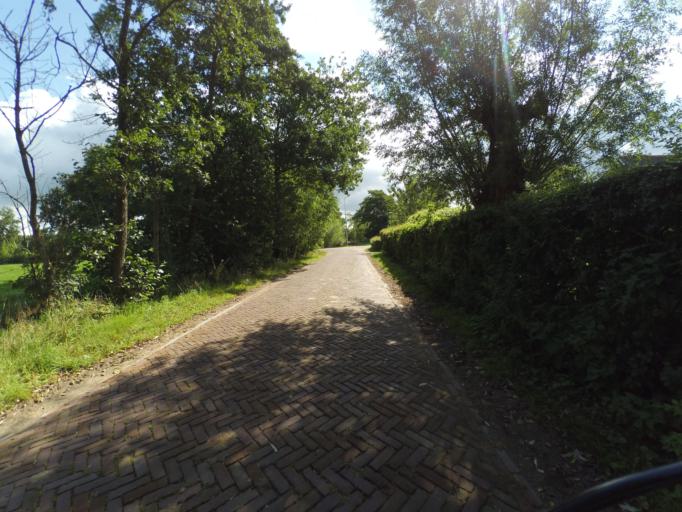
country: NL
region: Friesland
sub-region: Gemeente Tytsjerksteradiel
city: Noardburgum
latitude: 53.2050
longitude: 6.0145
